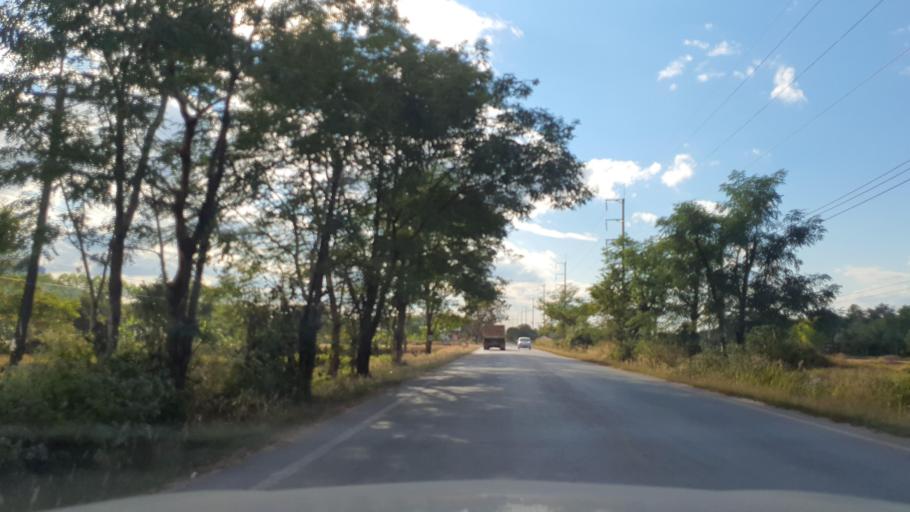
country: TH
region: Nakhon Phanom
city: Ban Phaeng
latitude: 18.0295
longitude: 104.1308
